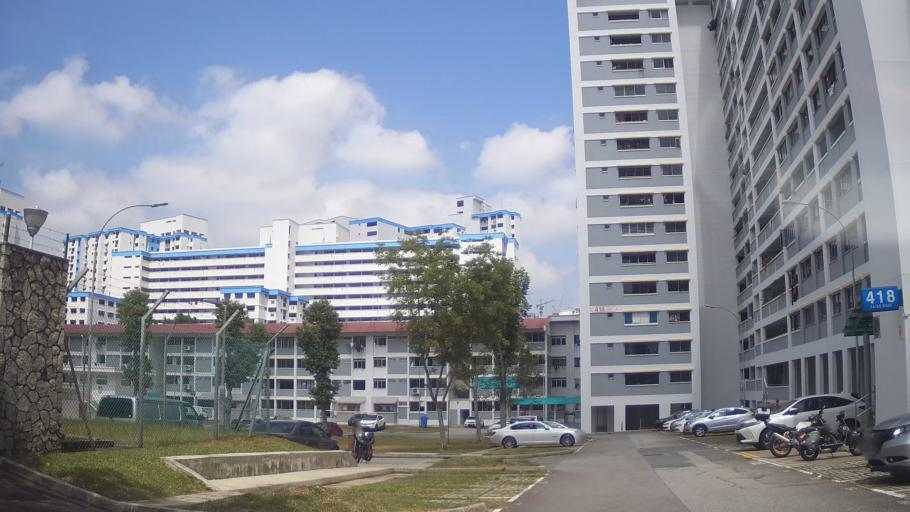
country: MY
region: Johor
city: Johor Bahru
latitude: 1.3839
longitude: 103.7691
